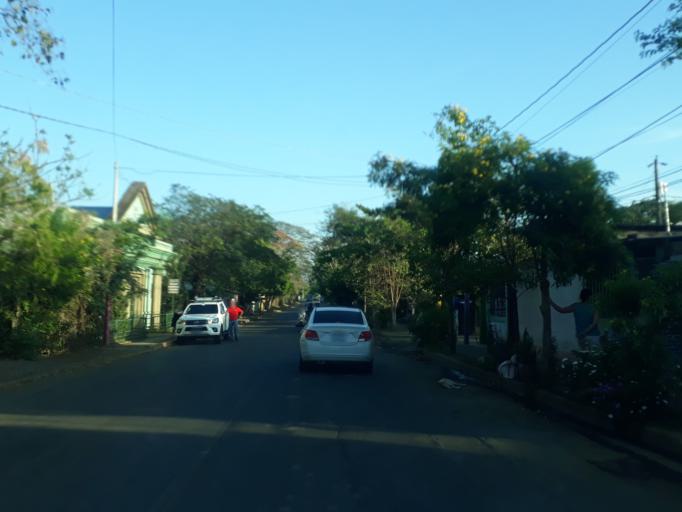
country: NI
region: Masaya
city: Masaya
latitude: 11.9899
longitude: -86.1063
